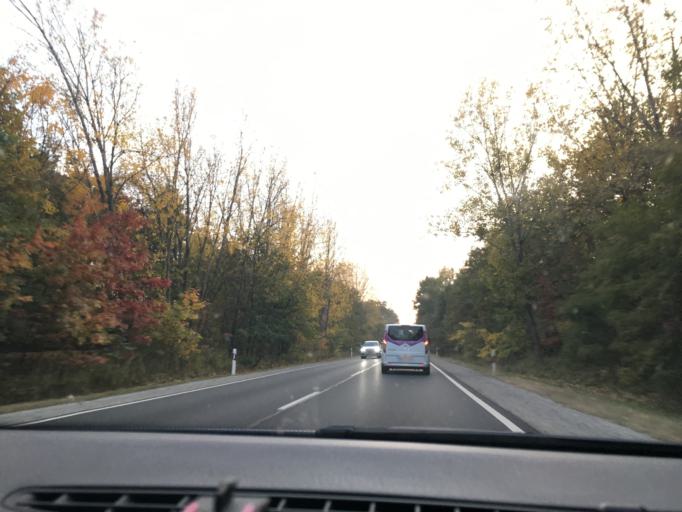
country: HU
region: Hajdu-Bihar
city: Teglas
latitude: 47.7209
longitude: 21.6691
